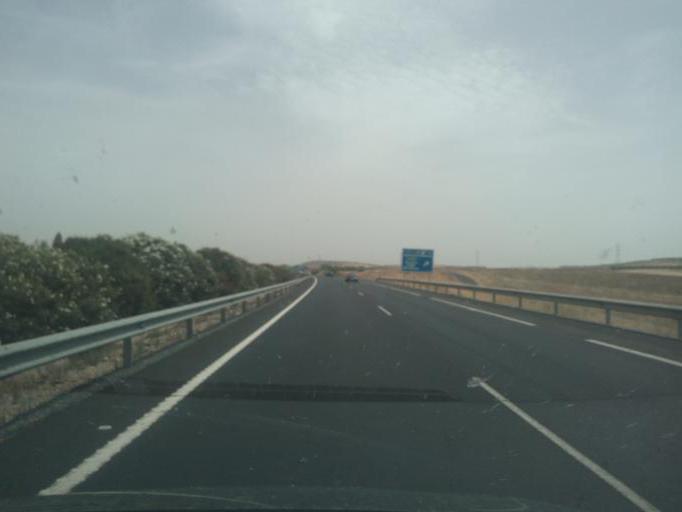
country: ES
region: Andalusia
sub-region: Provincia de Huelva
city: Bonares
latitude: 37.3412
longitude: -6.6915
